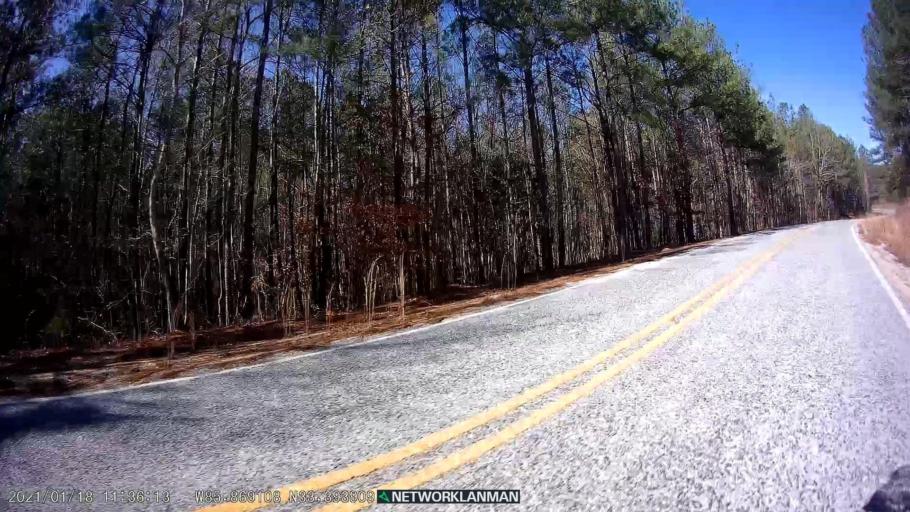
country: US
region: Alabama
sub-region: Clay County
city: Ashland
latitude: 33.3941
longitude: -85.8691
